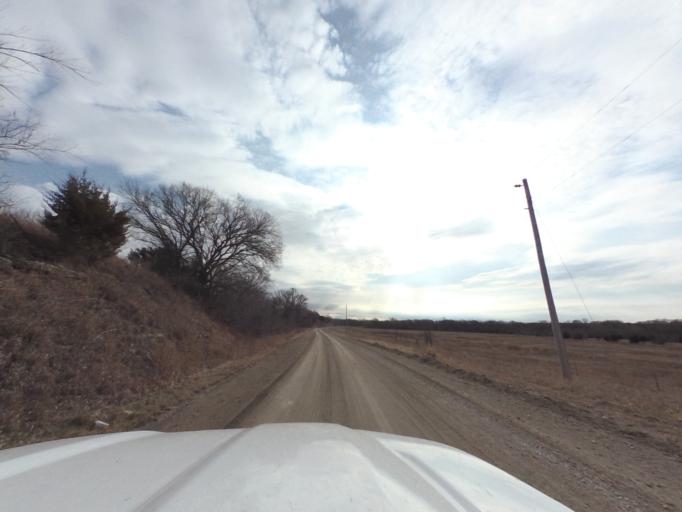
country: US
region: Kansas
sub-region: Chase County
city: Cottonwood Falls
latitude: 38.2692
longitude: -96.7310
